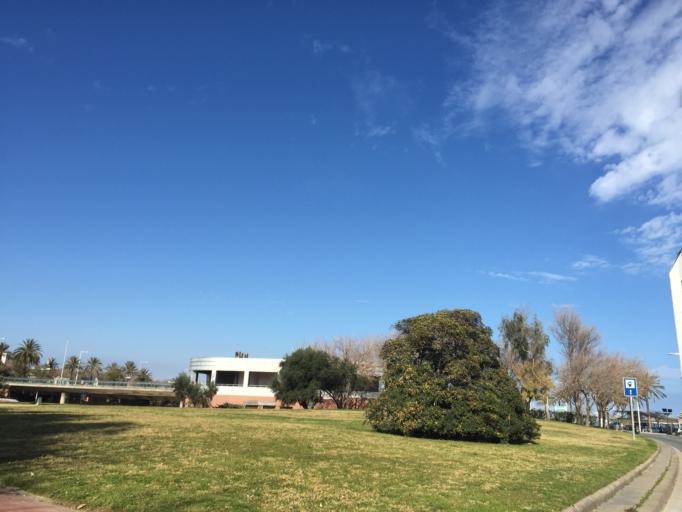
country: ES
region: Catalonia
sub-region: Provincia de Barcelona
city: Sant Marti
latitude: 41.3916
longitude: 2.2026
